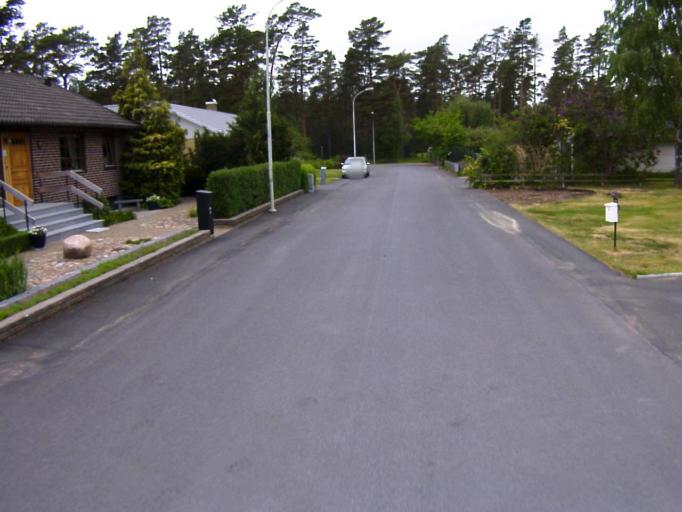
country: SE
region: Skane
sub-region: Kristianstads Kommun
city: Ahus
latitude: 55.9446
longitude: 14.2902
